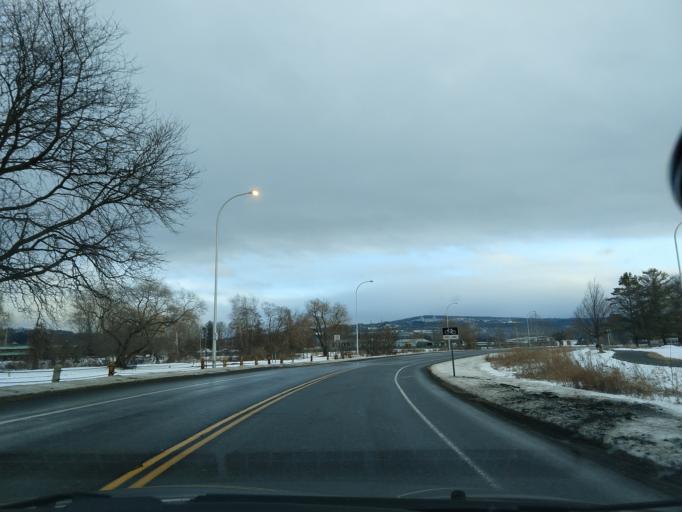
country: US
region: New York
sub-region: Tompkins County
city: Ithaca
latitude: 42.4514
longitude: -76.5125
